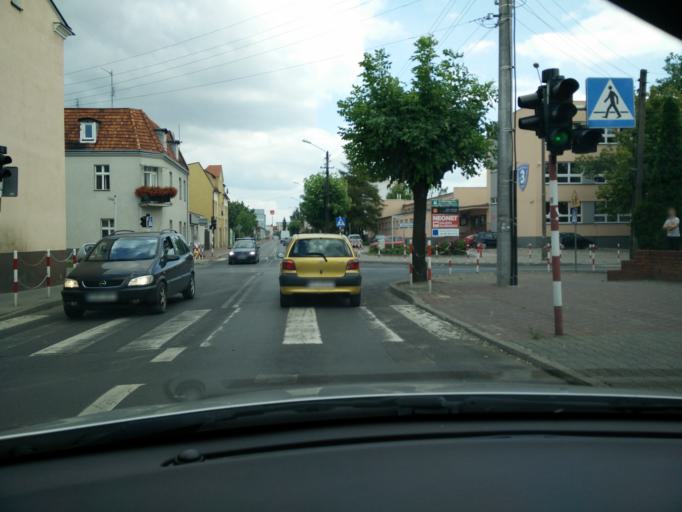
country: PL
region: Greater Poland Voivodeship
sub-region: Powiat sredzki
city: Sroda Wielkopolska
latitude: 52.2273
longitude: 17.2703
